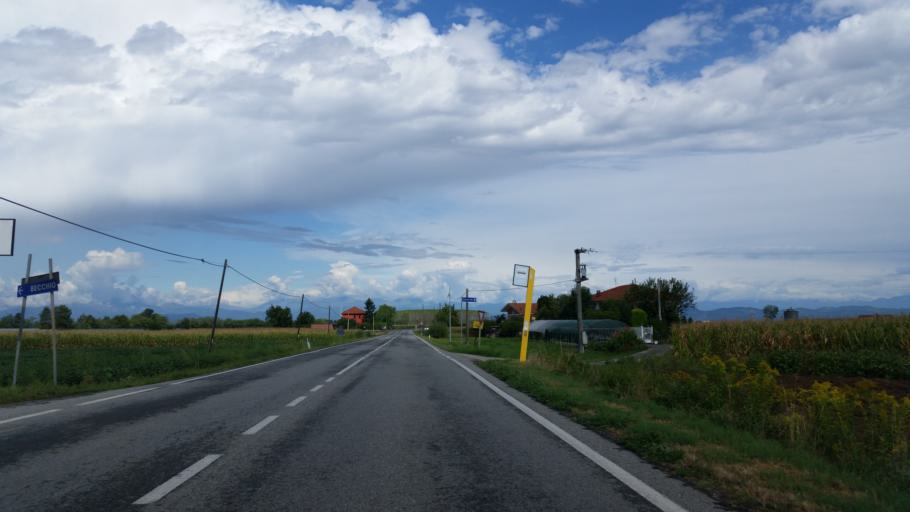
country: IT
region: Piedmont
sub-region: Provincia di Torino
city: Pralormo
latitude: 44.8854
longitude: 7.8729
